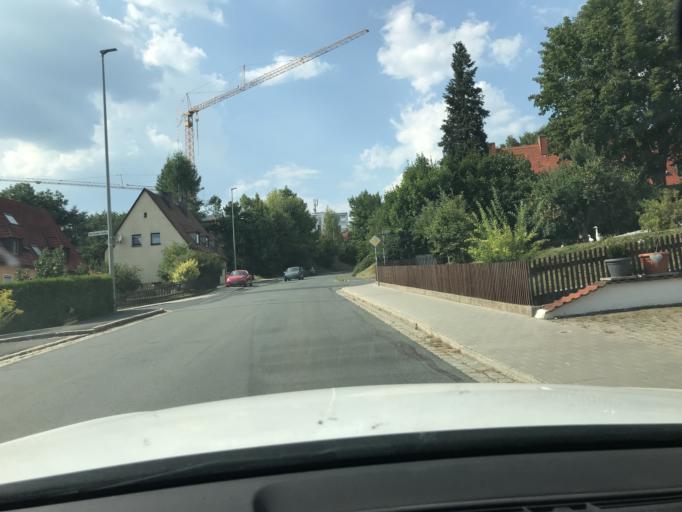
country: DE
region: Bavaria
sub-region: Upper Franconia
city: Pegnitz
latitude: 49.7449
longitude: 11.5417
